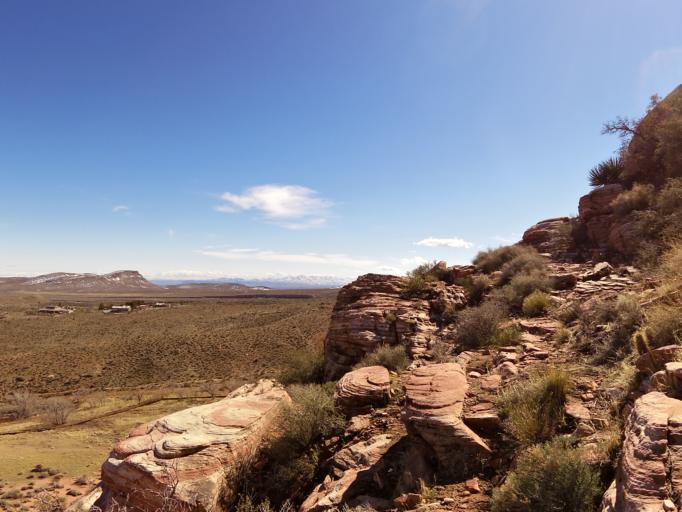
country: US
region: Nevada
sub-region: Clark County
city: Summerlin South
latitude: 36.1460
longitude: -115.4220
